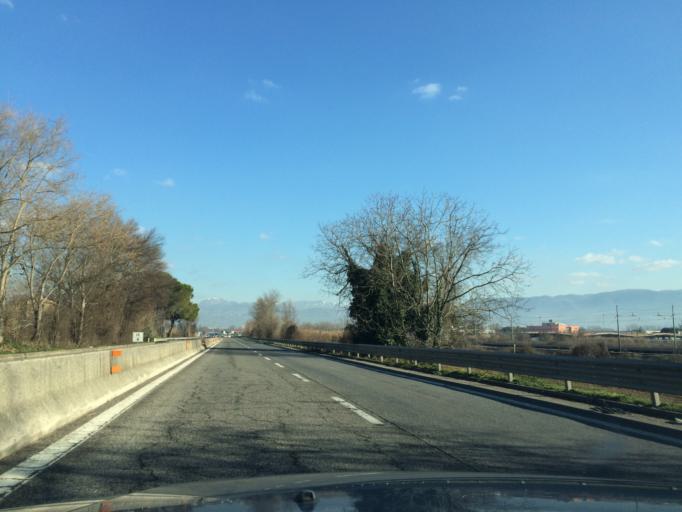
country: IT
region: Umbria
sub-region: Provincia di Terni
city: Terni
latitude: 42.5698
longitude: 12.6008
